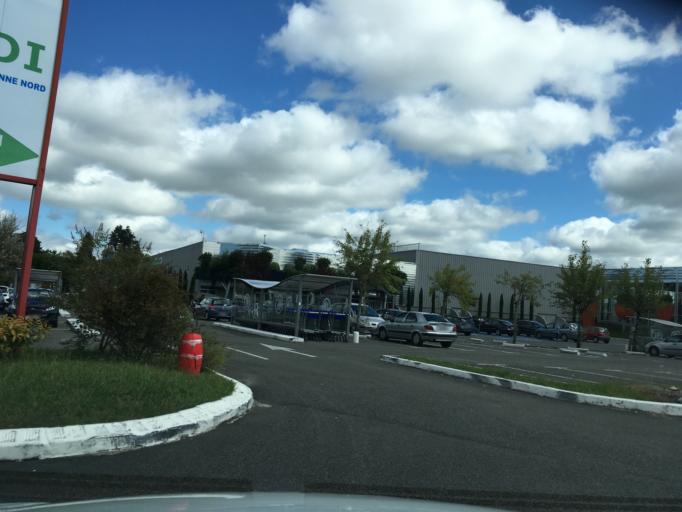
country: FR
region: Aquitaine
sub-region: Departement des Pyrenees-Atlantiques
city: Boucau
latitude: 43.5028
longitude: -1.4462
